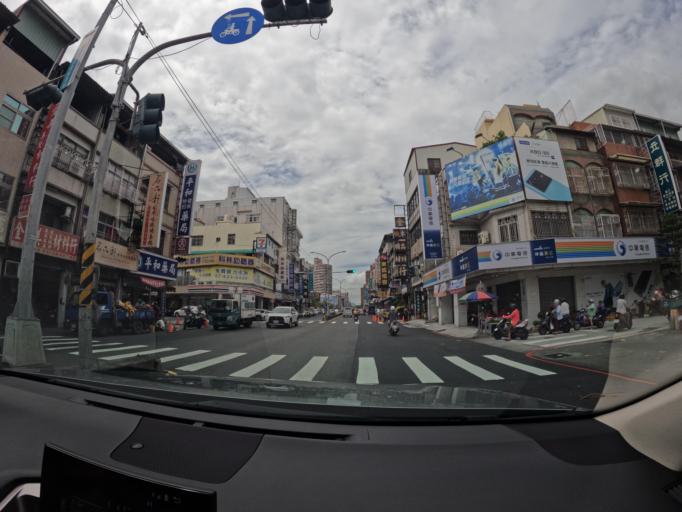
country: TW
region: Kaohsiung
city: Kaohsiung
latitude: 22.7930
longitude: 120.2959
